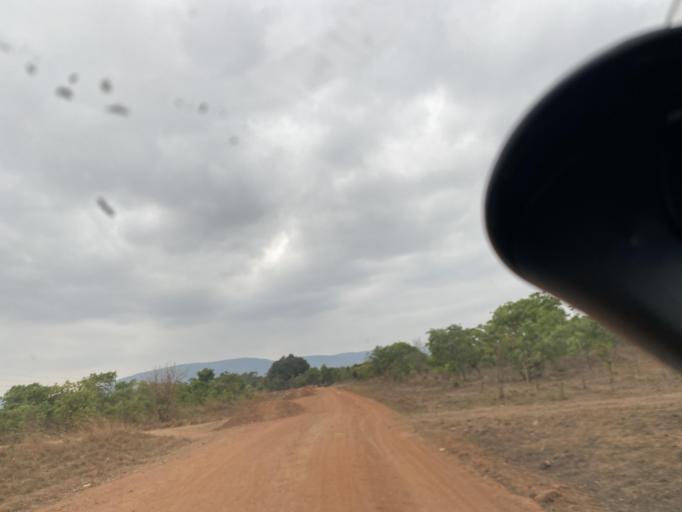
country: ZM
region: Lusaka
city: Chongwe
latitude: -15.2211
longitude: 28.7525
